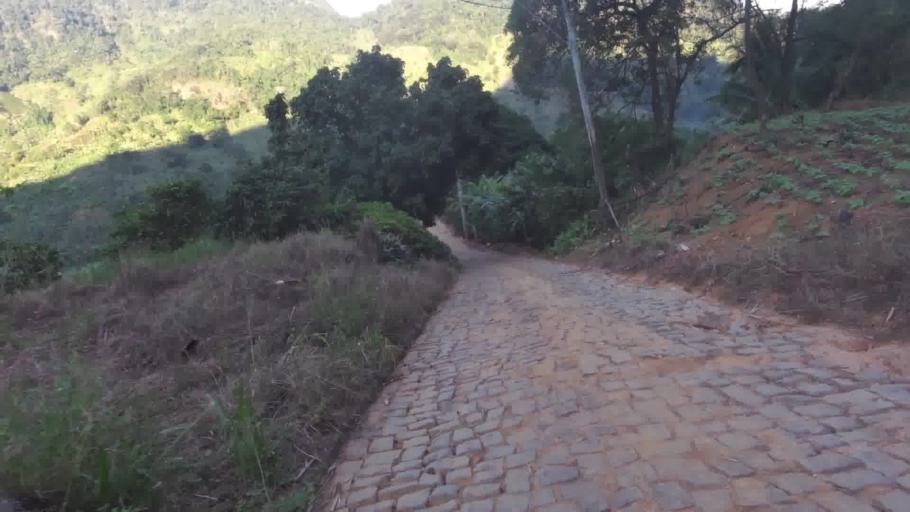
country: BR
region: Espirito Santo
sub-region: Alfredo Chaves
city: Alfredo Chaves
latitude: -20.5772
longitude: -40.7011
